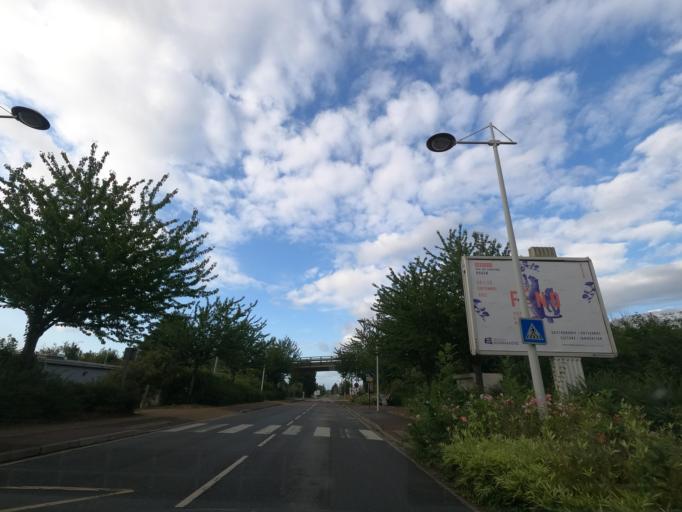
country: FR
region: Haute-Normandie
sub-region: Departement de la Seine-Maritime
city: Grand-Couronne
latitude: 49.3651
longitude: 1.0138
